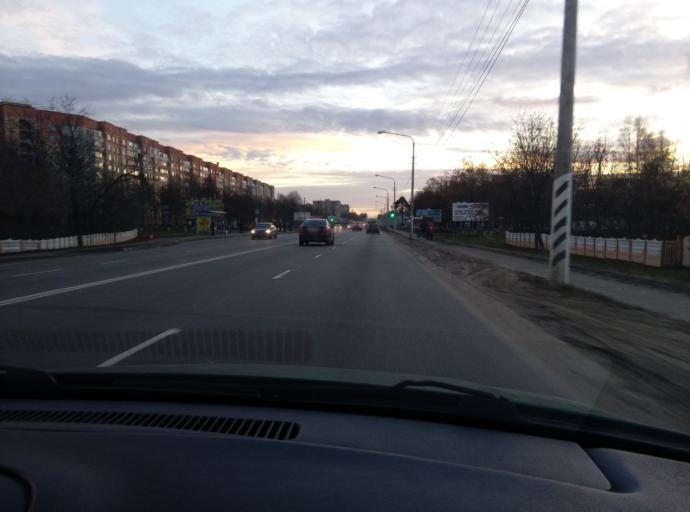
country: BY
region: Minsk
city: Horad Barysaw
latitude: 54.2244
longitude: 28.4940
